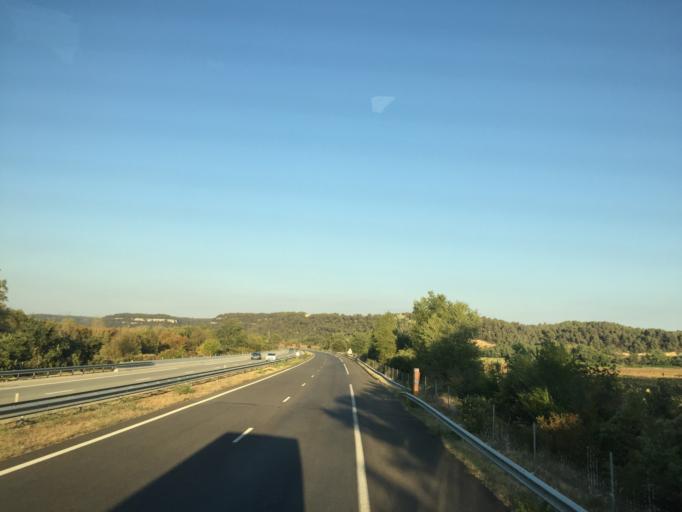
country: FR
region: Provence-Alpes-Cote d'Azur
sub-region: Departement des Bouches-du-Rhone
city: Peyrolles-en-Provence
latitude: 43.6562
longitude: 5.6003
